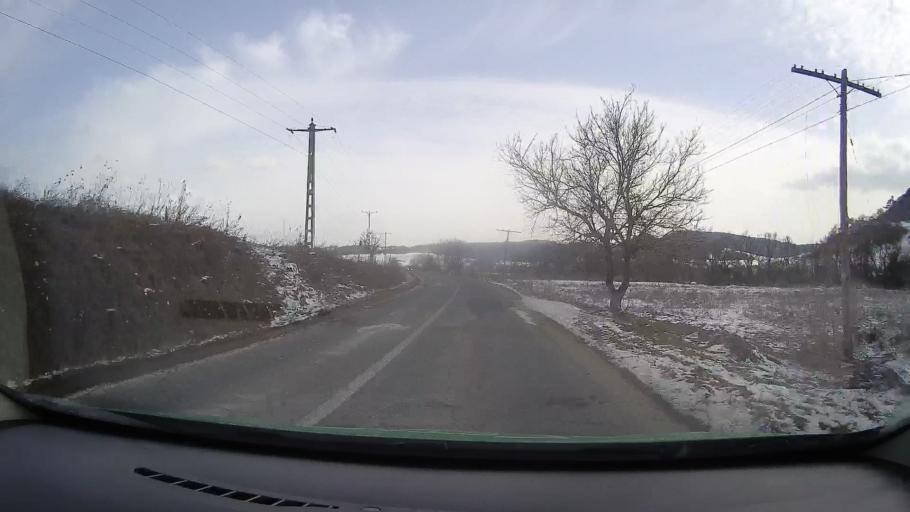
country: RO
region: Mures
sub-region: Comuna Apold
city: Saes
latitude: 46.1455
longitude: 24.7779
